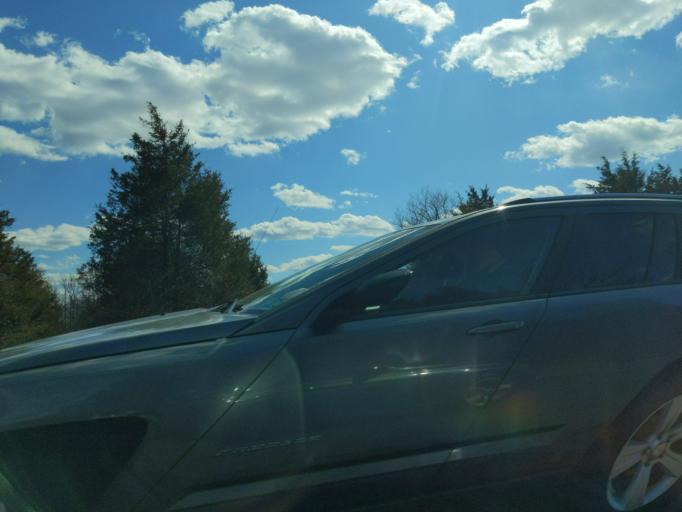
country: US
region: Pennsylvania
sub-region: Montgomery County
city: Pennsburg
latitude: 40.4120
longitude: -75.4676
